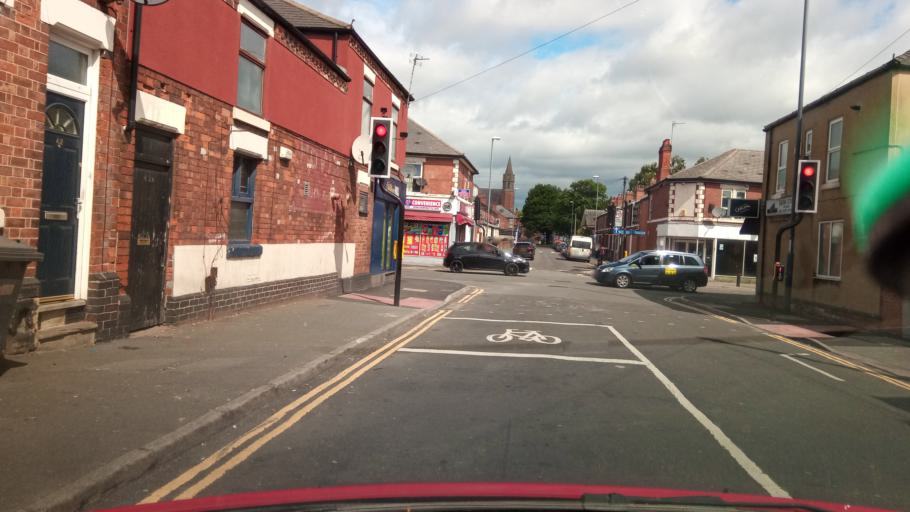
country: GB
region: England
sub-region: Derby
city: Derby
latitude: 52.9037
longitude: -1.4763
